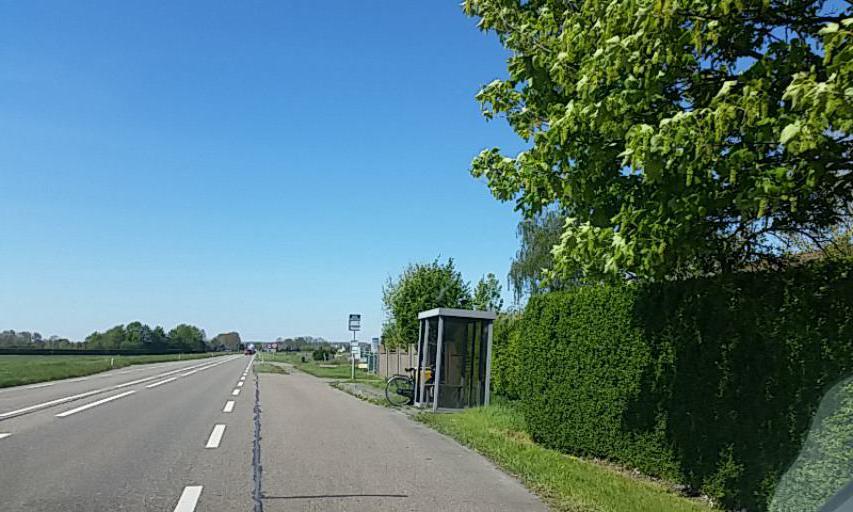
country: NL
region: Zeeland
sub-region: Gemeente Hulst
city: Hulst
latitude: 51.2718
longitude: 4.0191
